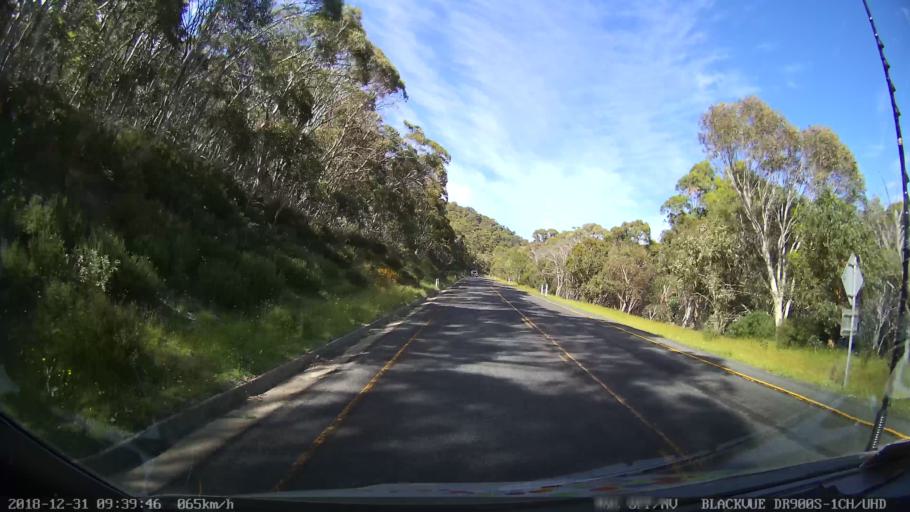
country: AU
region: New South Wales
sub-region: Snowy River
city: Jindabyne
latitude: -36.4803
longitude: 148.3510
